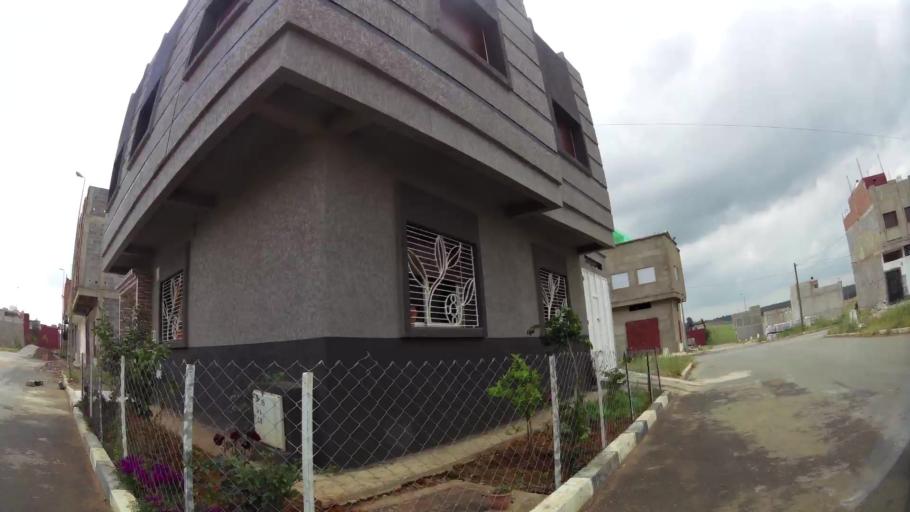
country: MA
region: Rabat-Sale-Zemmour-Zaer
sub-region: Khemisset
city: Tiflet
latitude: 33.8890
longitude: -6.3334
